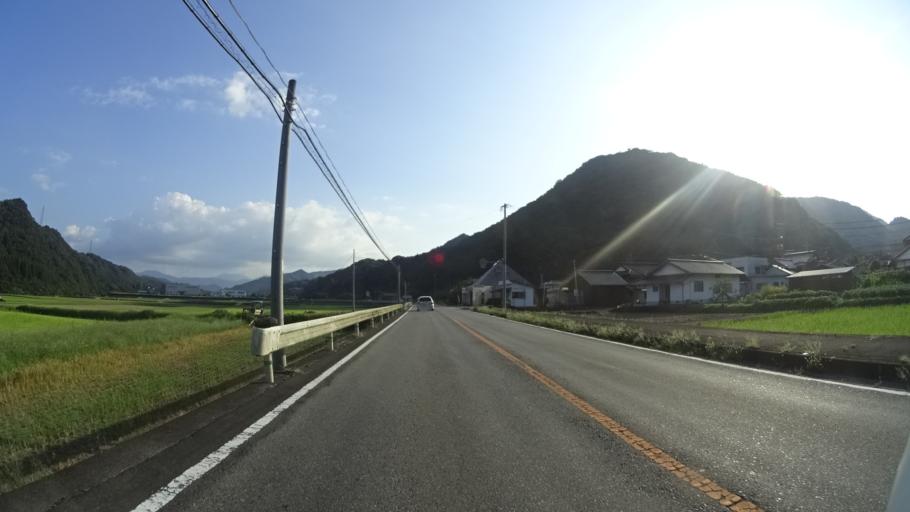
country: JP
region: Oita
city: Bungo-Takada-shi
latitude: 33.4738
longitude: 131.3290
